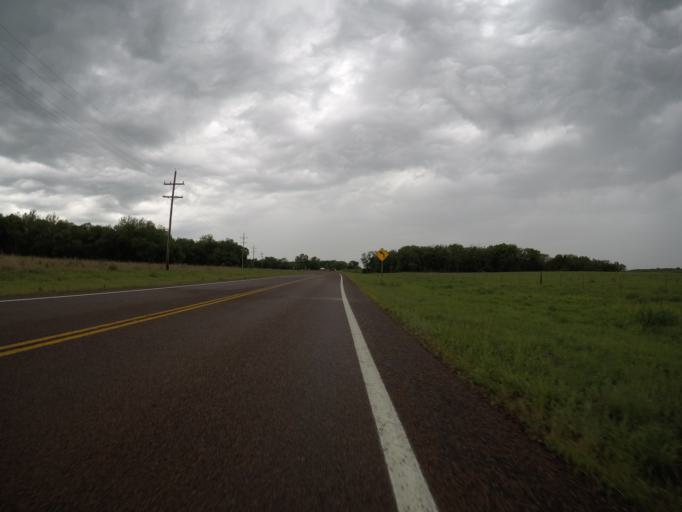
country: US
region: Kansas
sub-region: Shawnee County
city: Rossville
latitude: 38.9574
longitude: -96.0722
